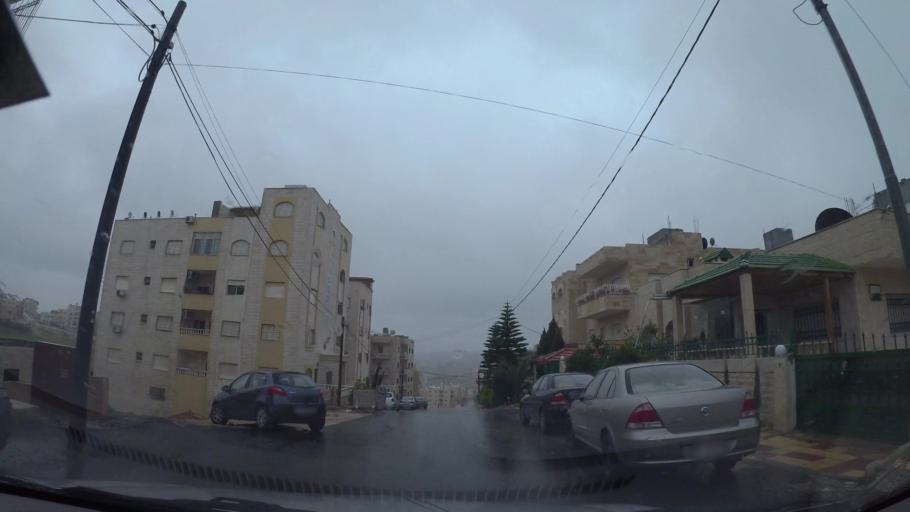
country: JO
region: Amman
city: Al Jubayhah
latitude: 32.0455
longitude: 35.8903
